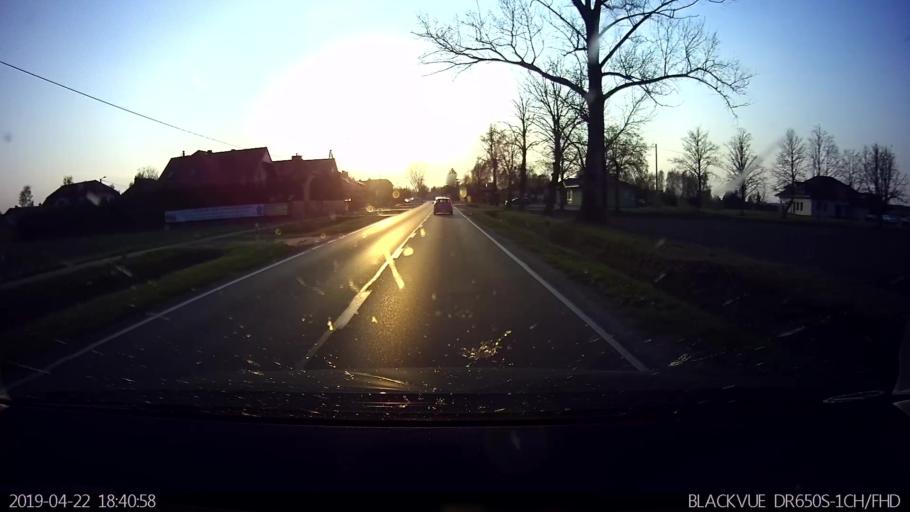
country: PL
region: Masovian Voivodeship
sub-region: Powiat wolominski
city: Dabrowka
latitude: 52.4473
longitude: 21.2706
